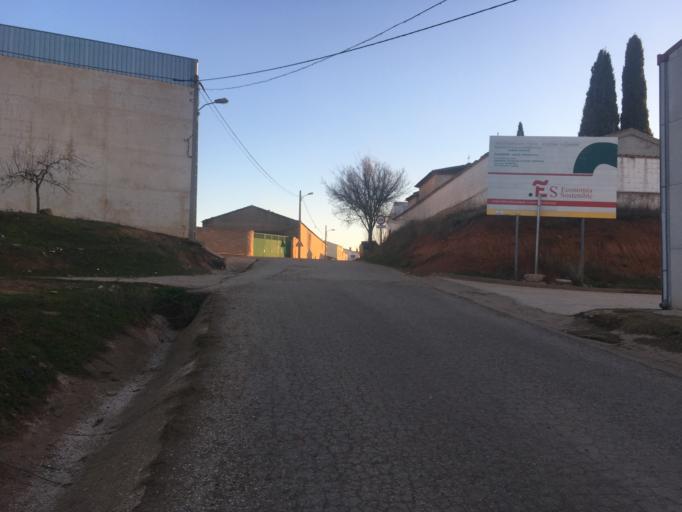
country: ES
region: Castille-La Mancha
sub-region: Provincia de Cuenca
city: Atalaya del Canavate
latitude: 39.5513
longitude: -2.2519
